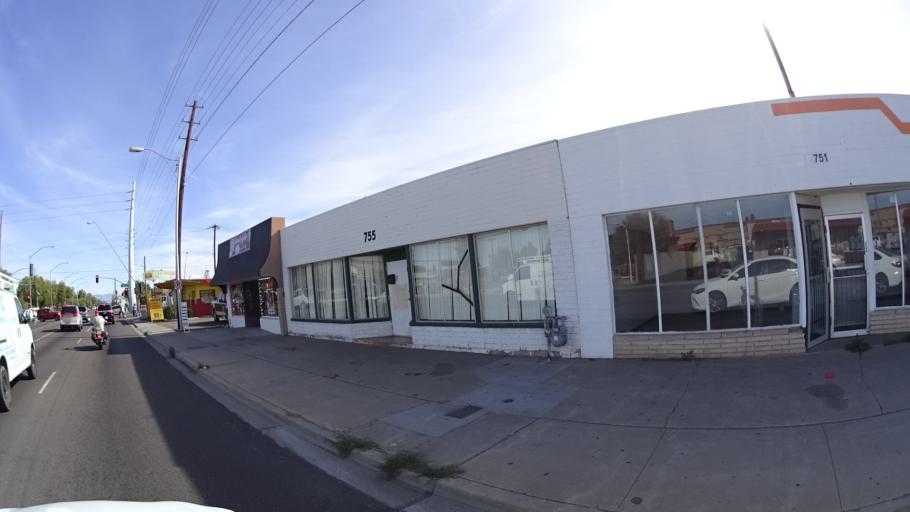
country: US
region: Arizona
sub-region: Maricopa County
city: Mesa
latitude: 33.4077
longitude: -111.8149
